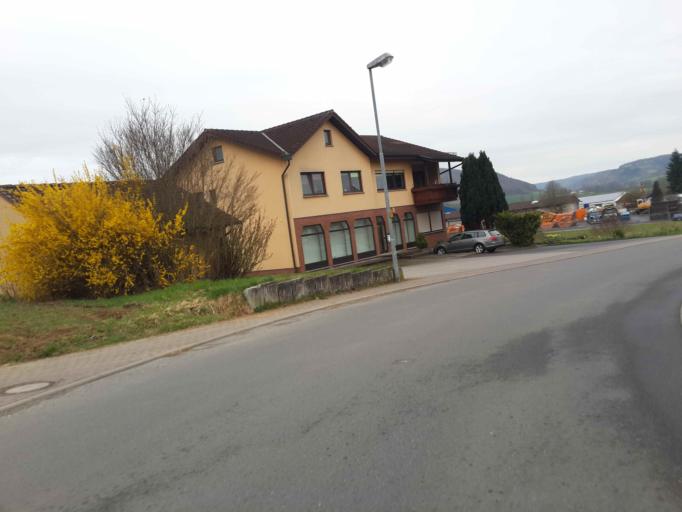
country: DE
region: Baden-Wuerttemberg
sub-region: Regierungsbezirk Stuttgart
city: Lauda-Konigshofen
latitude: 49.5437
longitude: 9.7394
